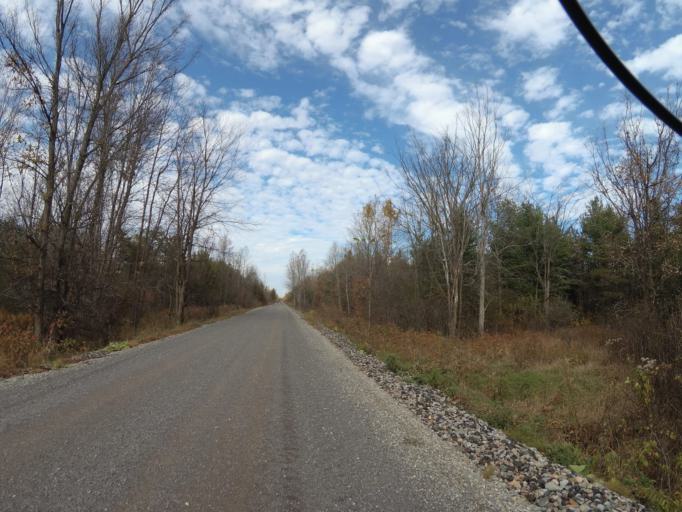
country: CA
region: Ontario
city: Carleton Place
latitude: 45.0724
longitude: -76.0997
